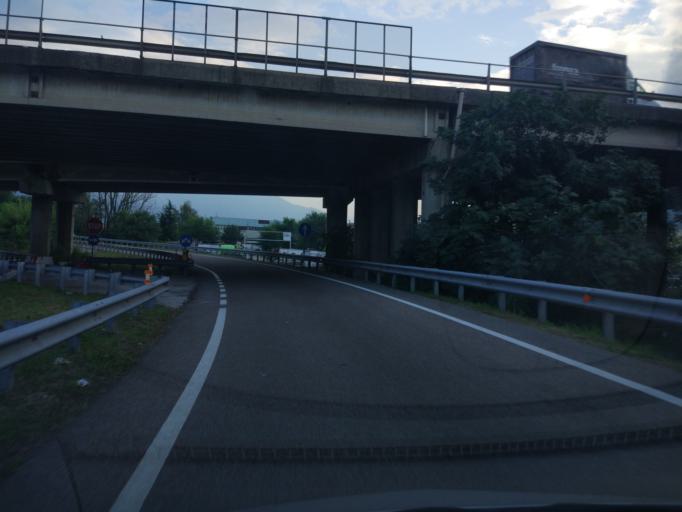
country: IT
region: Trentino-Alto Adige
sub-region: Provincia di Trento
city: Meano
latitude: 46.0960
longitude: 11.1112
